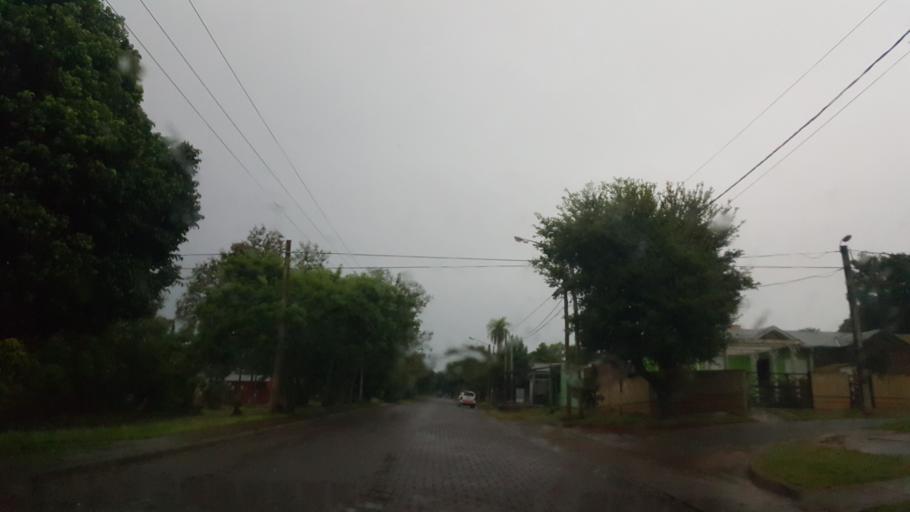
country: AR
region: Misiones
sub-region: Departamento de Capital
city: Posadas
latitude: -27.4149
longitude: -55.9552
